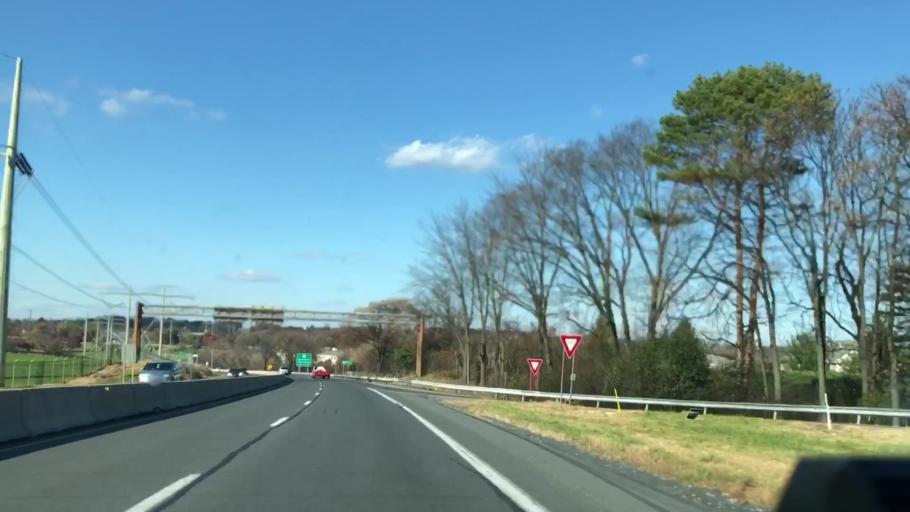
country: US
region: Pennsylvania
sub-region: Lehigh County
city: Wescosville
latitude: 40.5922
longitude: -75.5545
